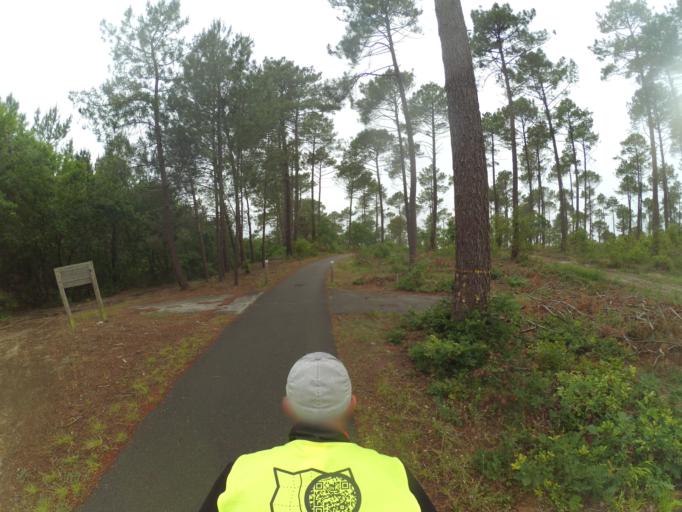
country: FR
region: Aquitaine
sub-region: Departement des Landes
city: Mimizan
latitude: 44.2185
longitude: -1.2498
